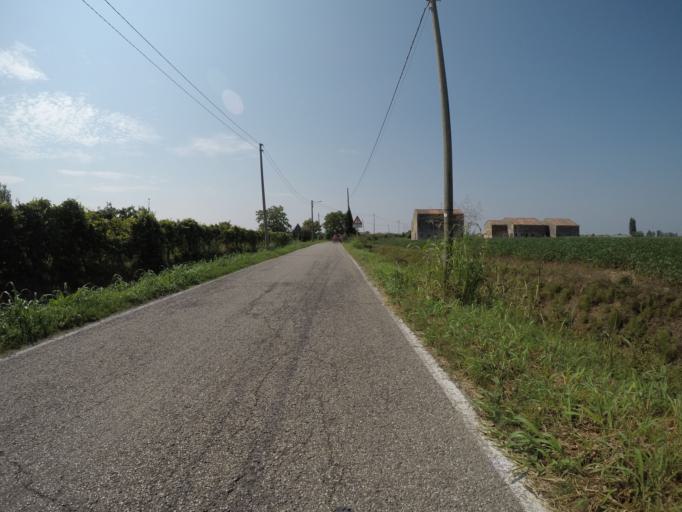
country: IT
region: Veneto
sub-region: Provincia di Rovigo
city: Lendinara
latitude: 45.1071
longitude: 11.5960
